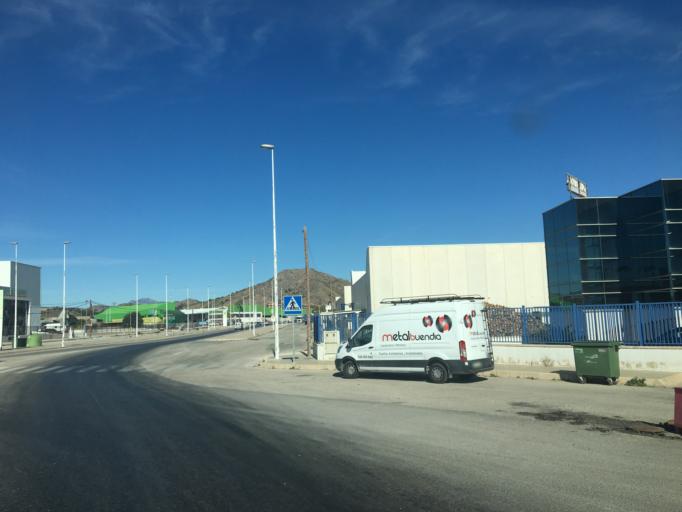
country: ES
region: Murcia
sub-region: Murcia
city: Santomera
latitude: 38.0755
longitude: -1.0573
